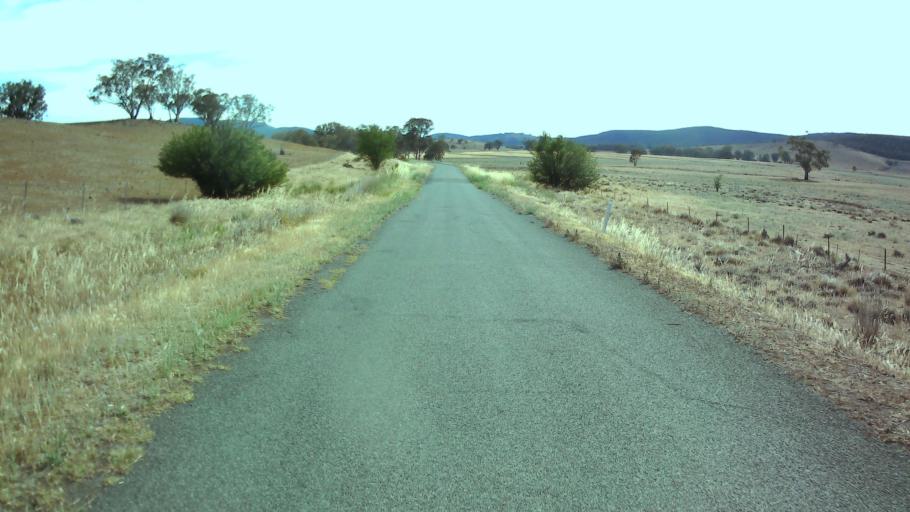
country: AU
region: New South Wales
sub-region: Weddin
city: Grenfell
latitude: -33.8254
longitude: 148.2870
